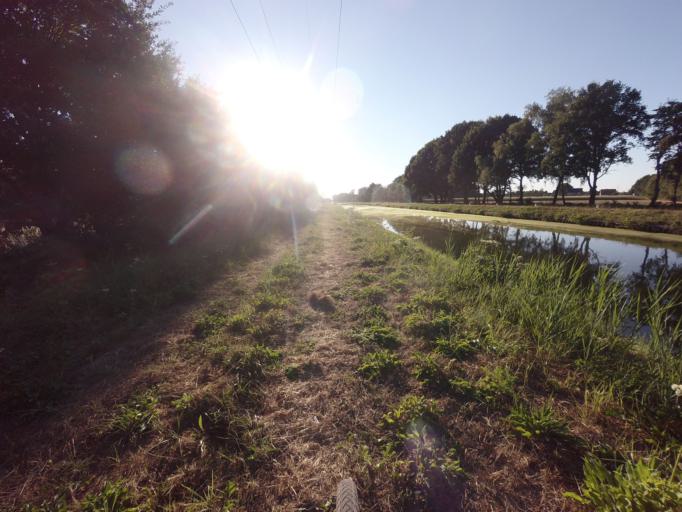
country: BE
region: Flanders
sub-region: Provincie Antwerpen
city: Oostmalle
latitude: 51.3401
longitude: 4.6984
